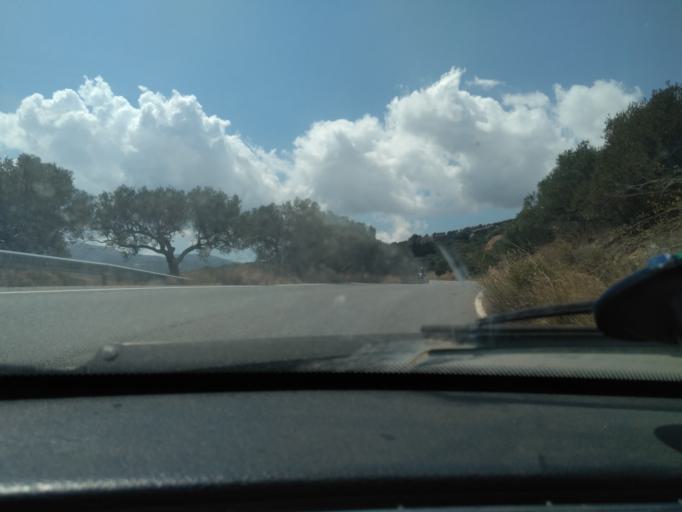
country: GR
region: Crete
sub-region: Nomos Lasithiou
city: Siteia
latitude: 35.1389
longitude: 26.0763
